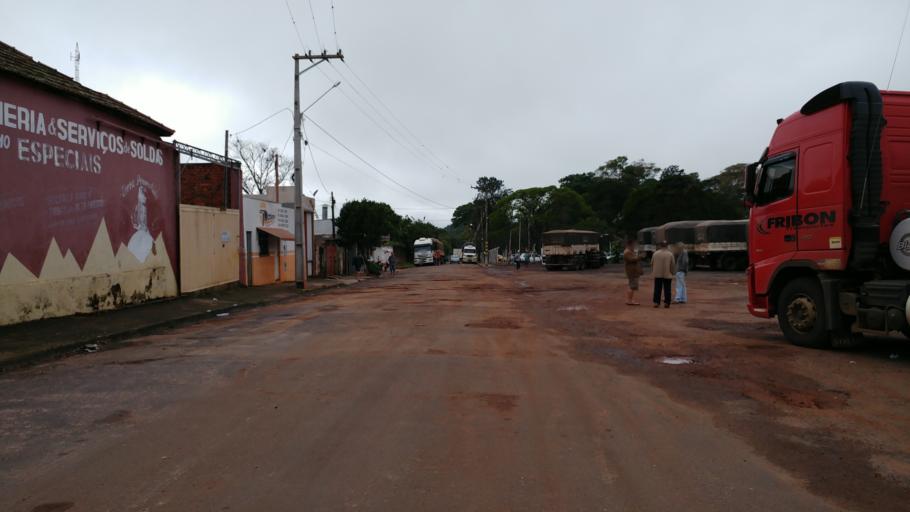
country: BR
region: Sao Paulo
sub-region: Paraguacu Paulista
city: Paraguacu Paulista
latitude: -22.4205
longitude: -50.5724
